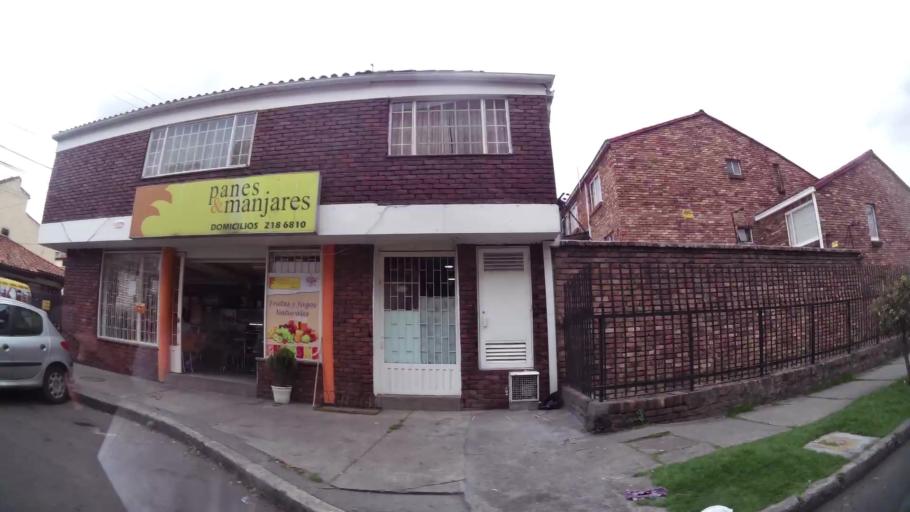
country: CO
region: Bogota D.C.
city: Barrio San Luis
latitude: 4.6843
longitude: -74.0690
